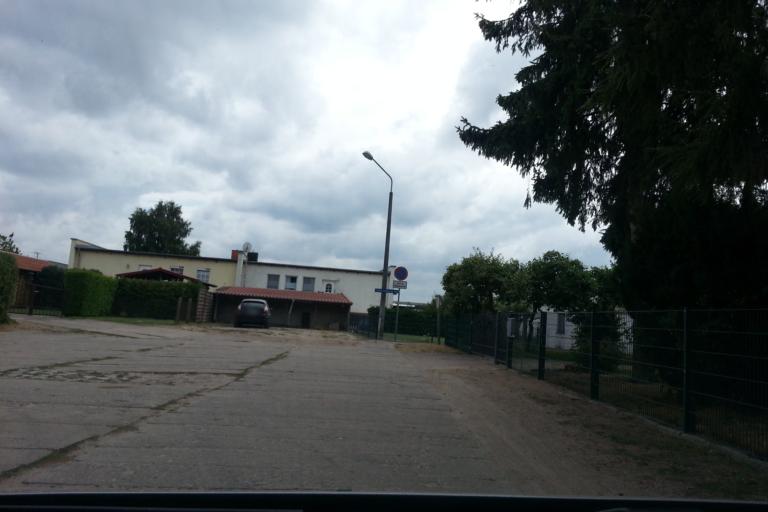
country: DE
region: Mecklenburg-Vorpommern
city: Ferdinandshof
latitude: 53.6609
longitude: 13.8946
